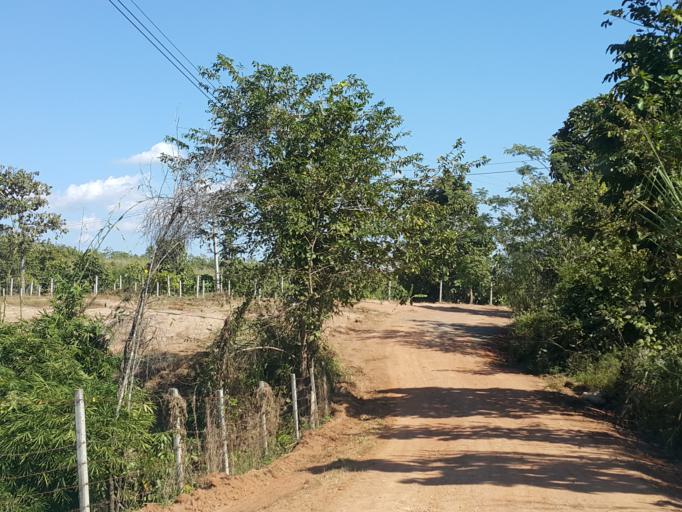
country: TH
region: Chiang Mai
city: Mae Taeng
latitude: 18.9512
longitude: 98.9054
